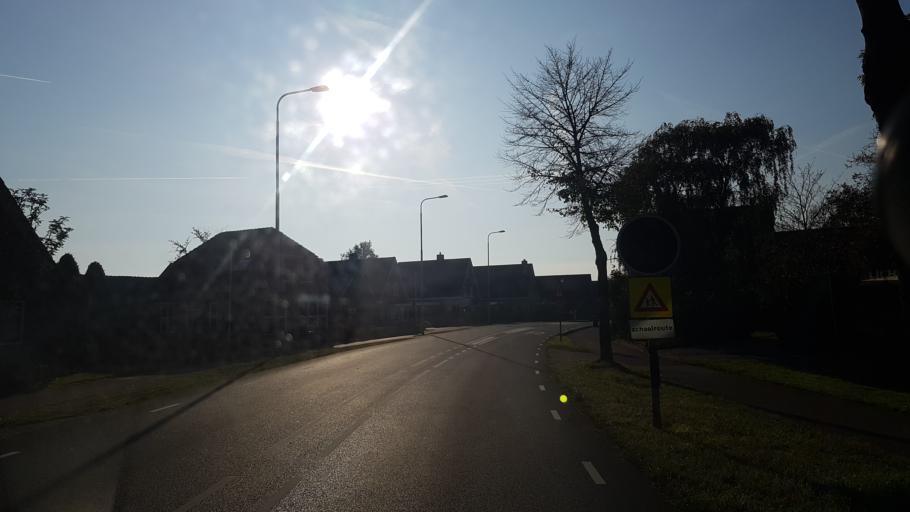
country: NL
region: Gelderland
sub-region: Gemeente Brummen
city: Eerbeek
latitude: 52.1684
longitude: 6.0652
